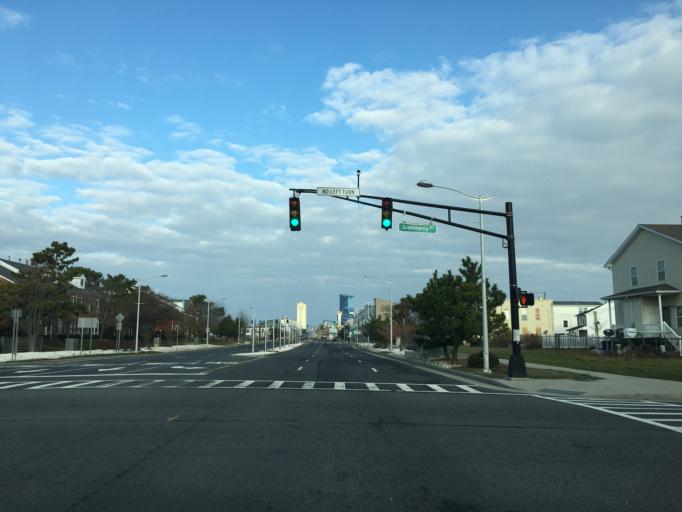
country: US
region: New Jersey
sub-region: Atlantic County
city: Atlantic City
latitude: 39.3677
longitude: -74.4188
